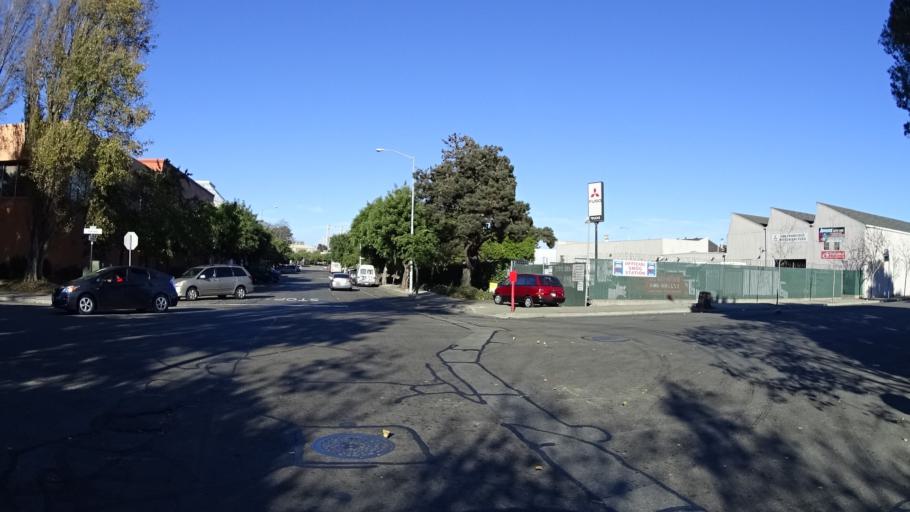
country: US
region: California
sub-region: San Francisco County
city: San Francisco
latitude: 37.7406
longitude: -122.3878
